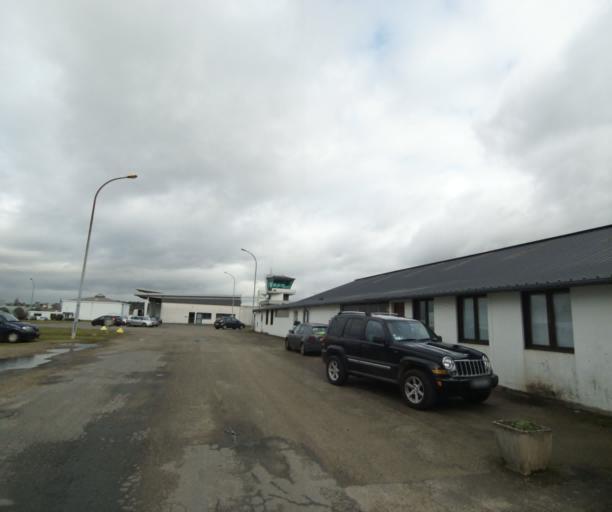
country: FR
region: Pays de la Loire
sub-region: Departement de la Sarthe
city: Arnage
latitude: 47.9458
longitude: 0.1961
